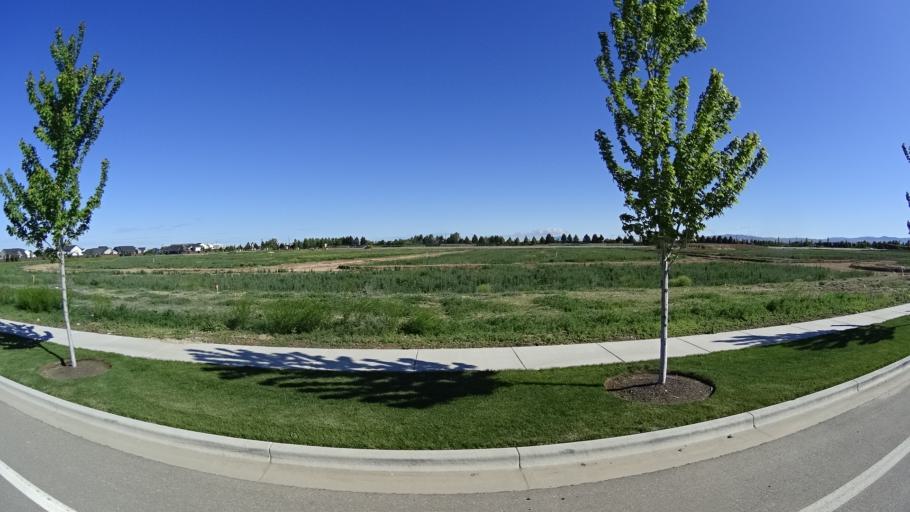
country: US
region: Idaho
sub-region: Ada County
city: Star
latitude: 43.6600
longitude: -116.4409
